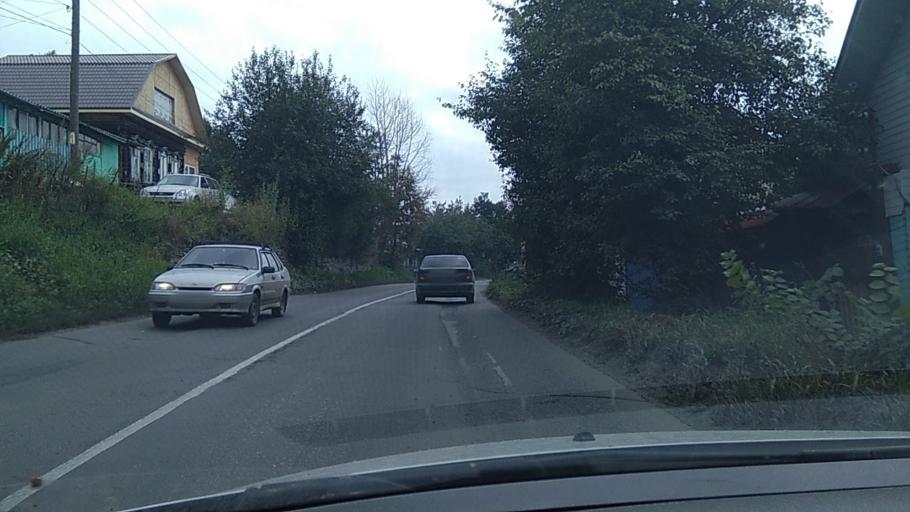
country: RU
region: Chelyabinsk
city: Zlatoust
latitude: 55.1759
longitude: 59.6896
